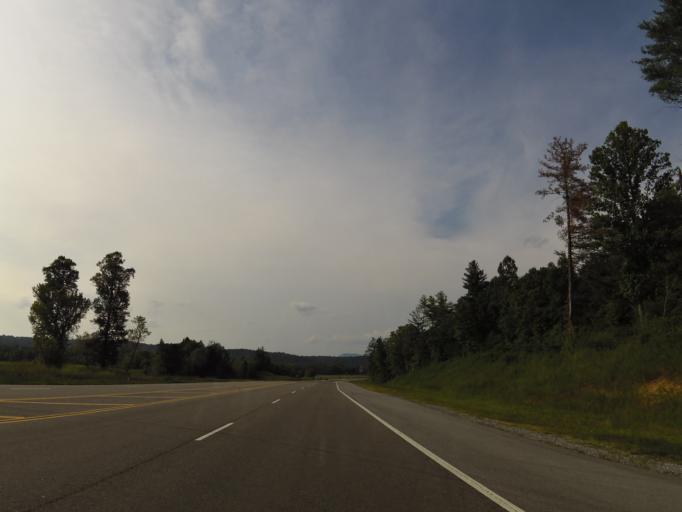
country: US
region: Tennessee
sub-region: Roane County
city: Oliver Springs
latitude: 35.9499
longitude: -84.3632
